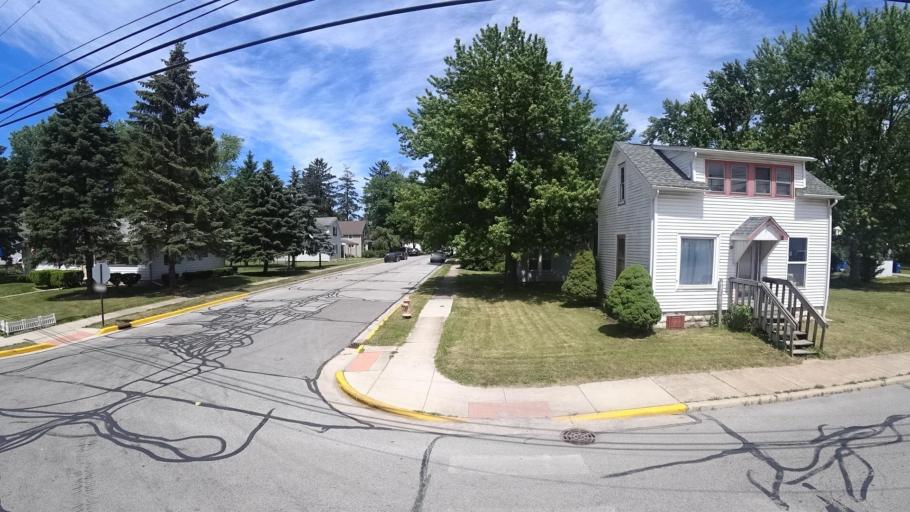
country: US
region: Indiana
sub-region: Porter County
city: Porter
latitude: 41.6149
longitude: -87.0754
